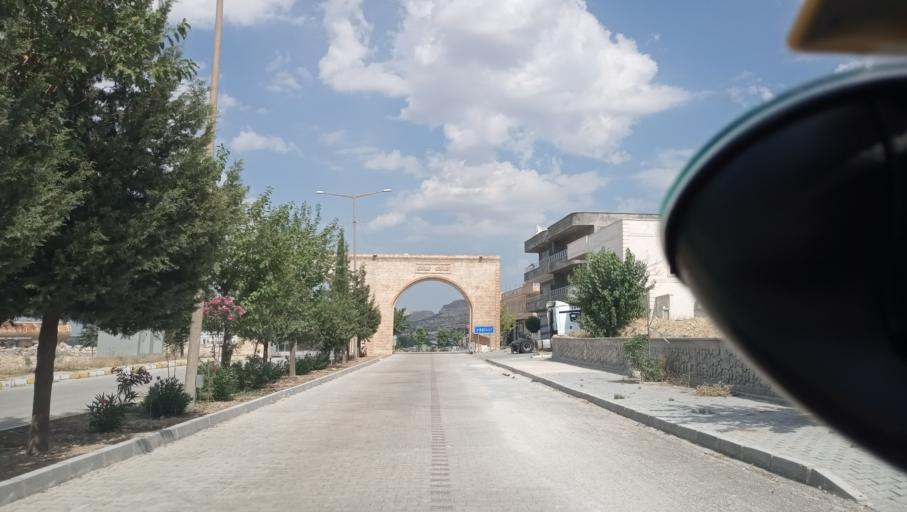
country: TR
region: Mardin
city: Kabala
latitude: 37.3428
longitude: 40.8058
